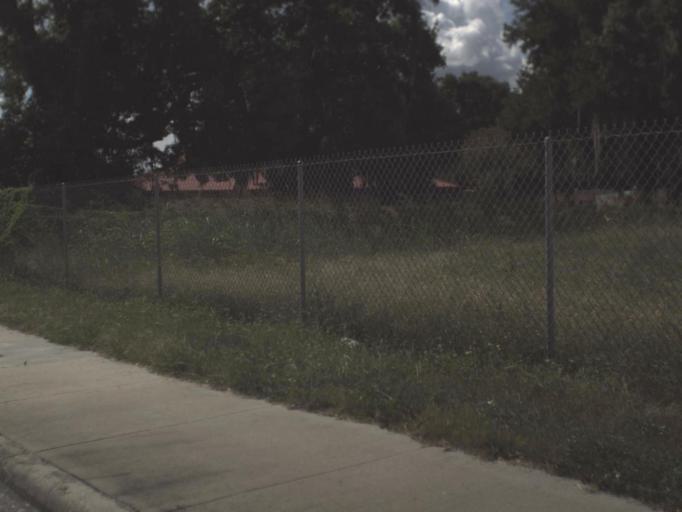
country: US
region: Florida
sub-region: Polk County
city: Winston
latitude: 28.0422
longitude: -81.9860
